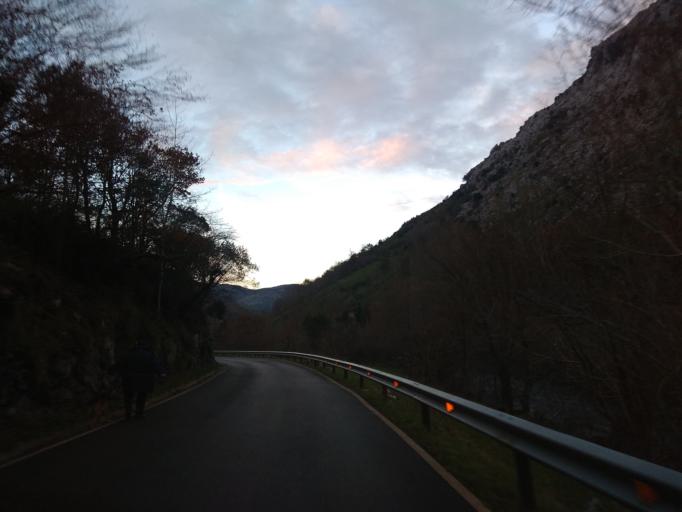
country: ES
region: Cantabria
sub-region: Provincia de Cantabria
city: Arredondo
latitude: 43.2499
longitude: -3.6061
